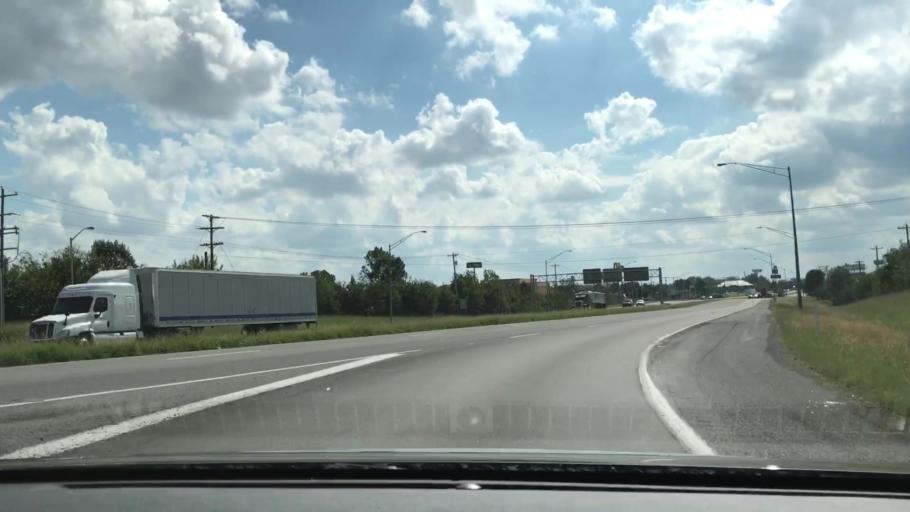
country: US
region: Kentucky
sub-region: Christian County
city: Oak Grove
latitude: 36.7007
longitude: -87.4547
